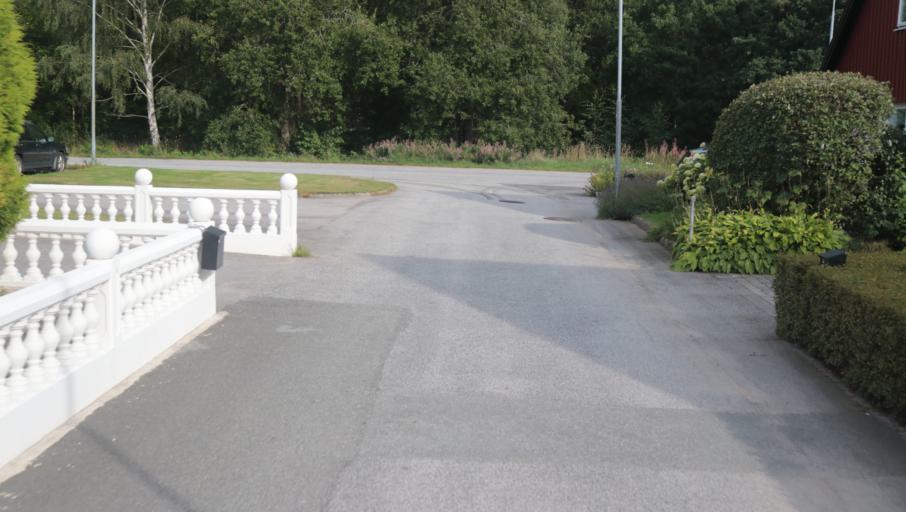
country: SE
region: Blekinge
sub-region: Karlshamns Kommun
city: Karlshamn
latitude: 56.2087
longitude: 14.8508
